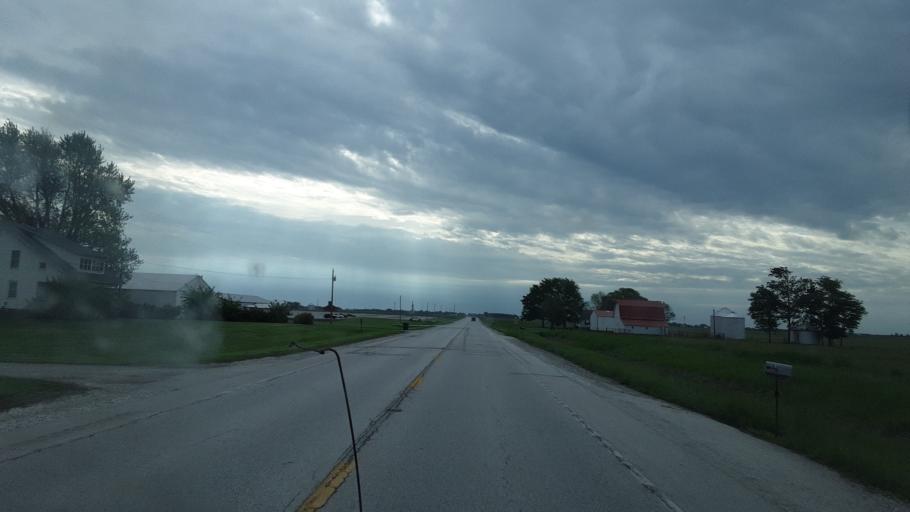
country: US
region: Illinois
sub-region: Hancock County
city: Hamilton
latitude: 40.3958
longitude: -91.3028
